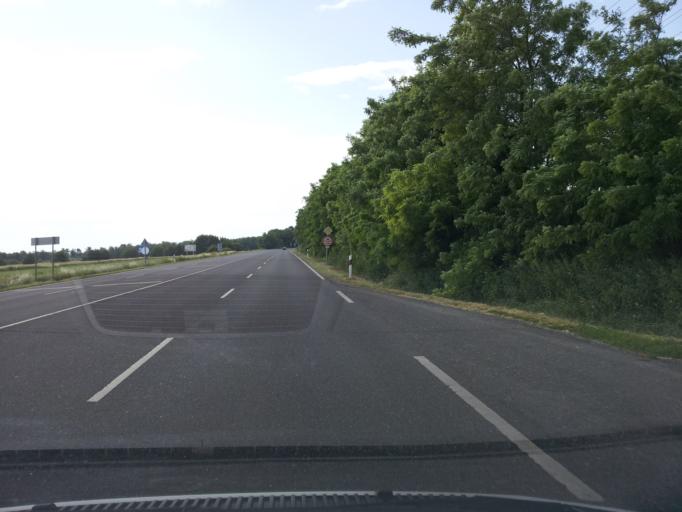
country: HU
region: Veszprem
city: Veszprem
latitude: 47.0612
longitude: 17.9246
